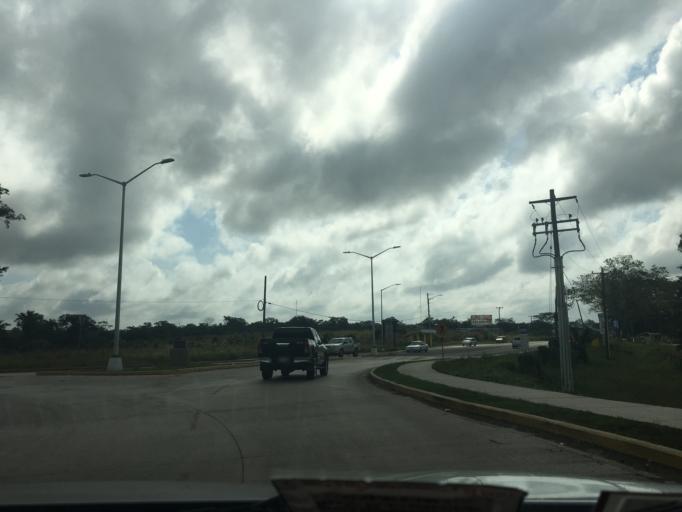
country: BZ
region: Cayo
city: Belmopan
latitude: 17.2611
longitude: -88.7876
